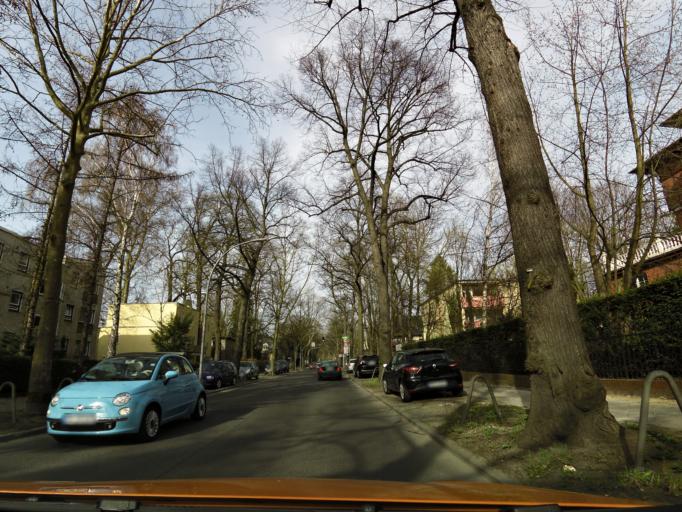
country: DE
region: Berlin
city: Lichterfelde
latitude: 52.4327
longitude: 13.3187
